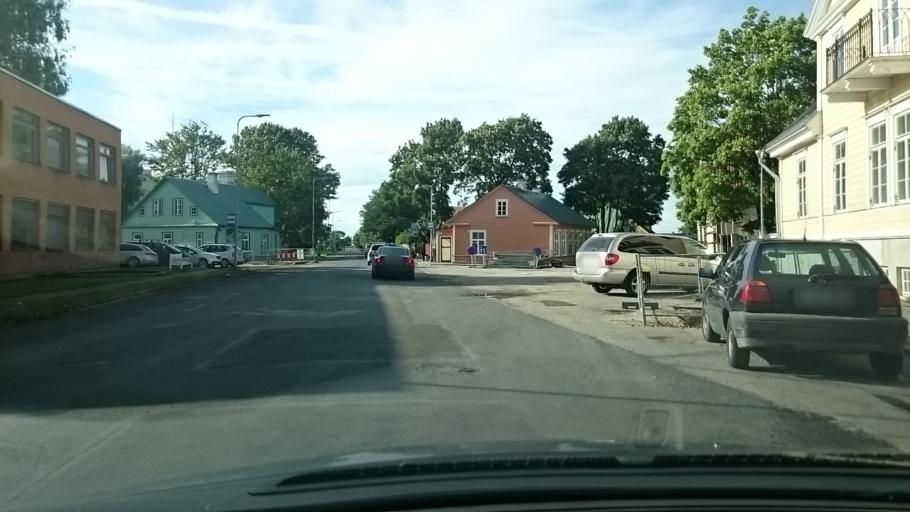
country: EE
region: Laeaene
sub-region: Haapsalu linn
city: Haapsalu
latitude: 58.9469
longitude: 23.5311
